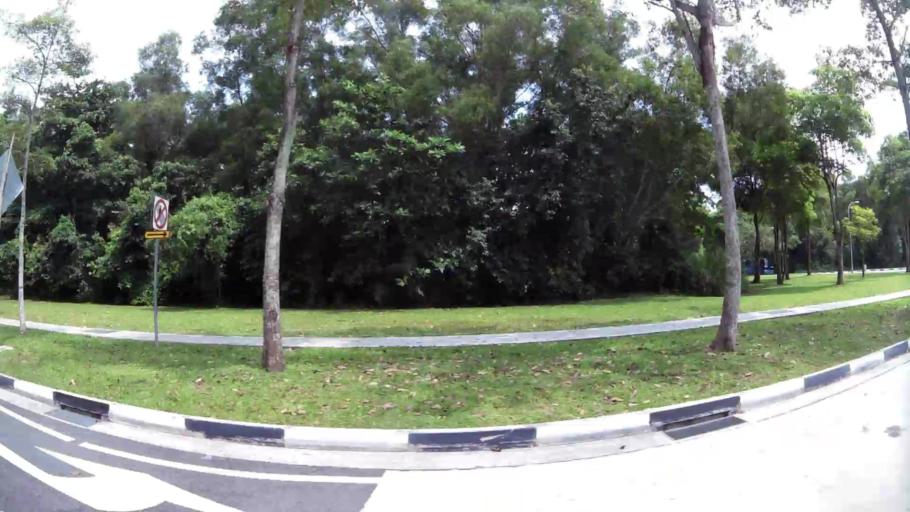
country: MY
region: Johor
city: Kampung Pasir Gudang Baru
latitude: 1.3757
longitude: 103.9481
